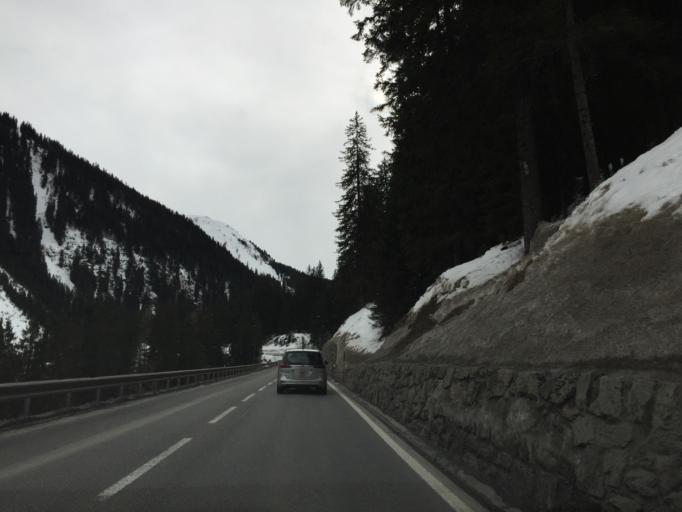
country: CH
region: Grisons
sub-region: Praettigau/Davos District
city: Klosters Serneus
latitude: 46.8506
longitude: 9.8829
